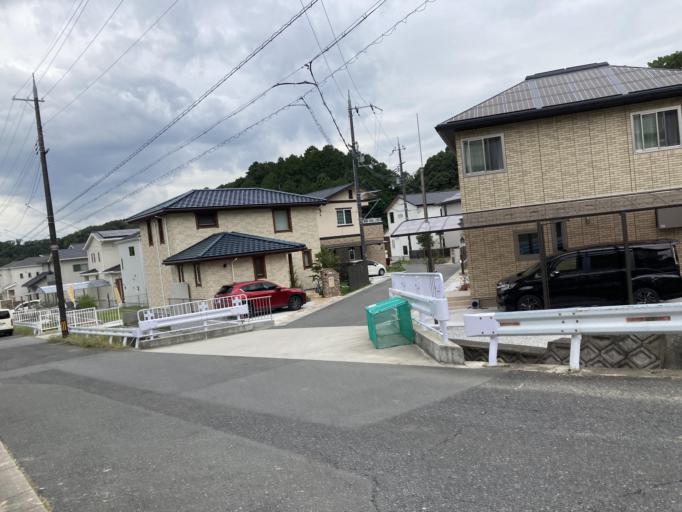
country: JP
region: Nara
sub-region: Ikoma-shi
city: Ikoma
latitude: 34.6828
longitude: 135.6986
